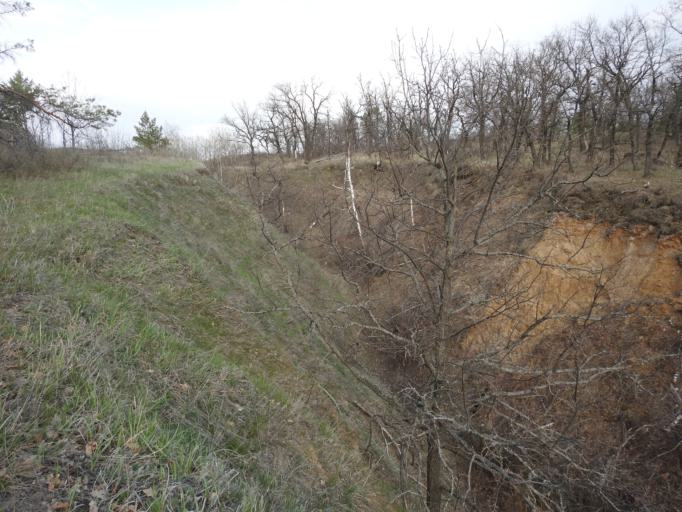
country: RU
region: Saratov
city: Krasnyy Oktyabr'
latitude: 51.4152
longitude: 45.5447
